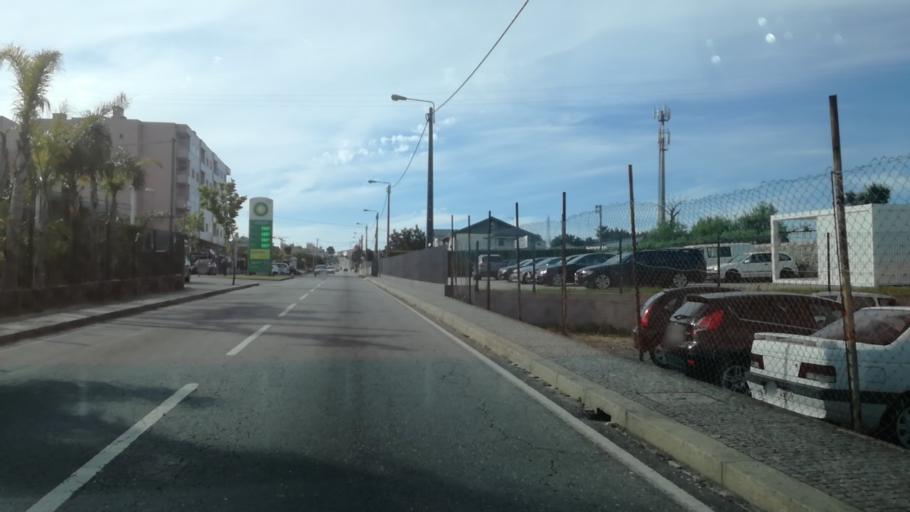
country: PT
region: Porto
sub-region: Valongo
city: Ermesinde
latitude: 41.2273
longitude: -8.5671
